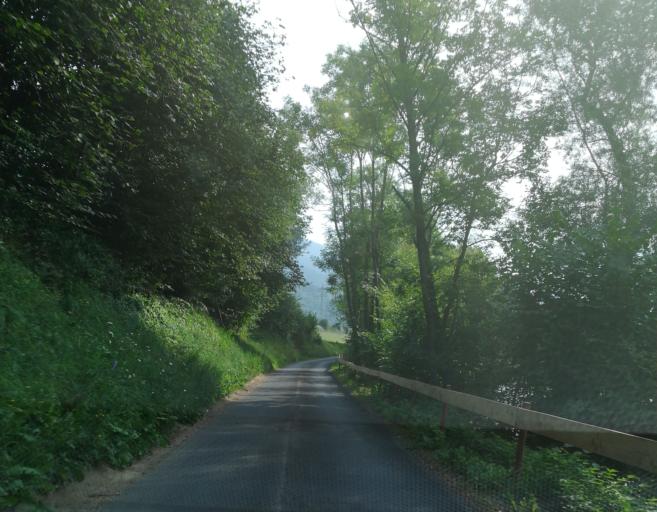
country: AT
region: Styria
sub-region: Politischer Bezirk Murtal
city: Sankt Georgen ob Judenburg
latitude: 47.2111
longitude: 14.4581
